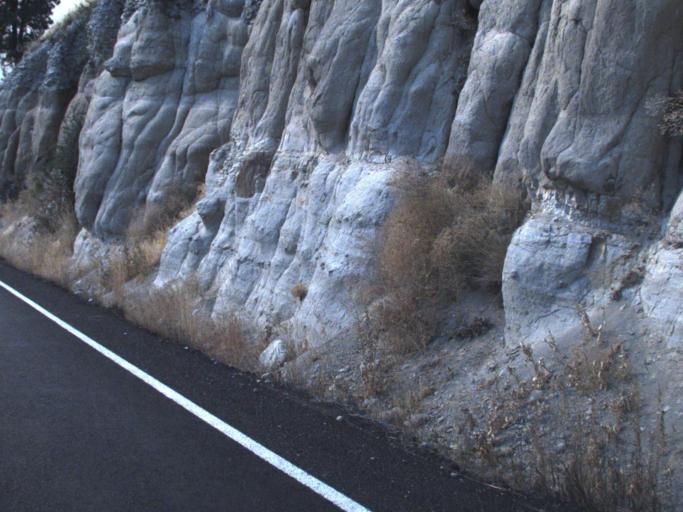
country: US
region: Washington
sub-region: Kittitas County
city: Cle Elum
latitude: 47.1653
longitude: -120.8152
